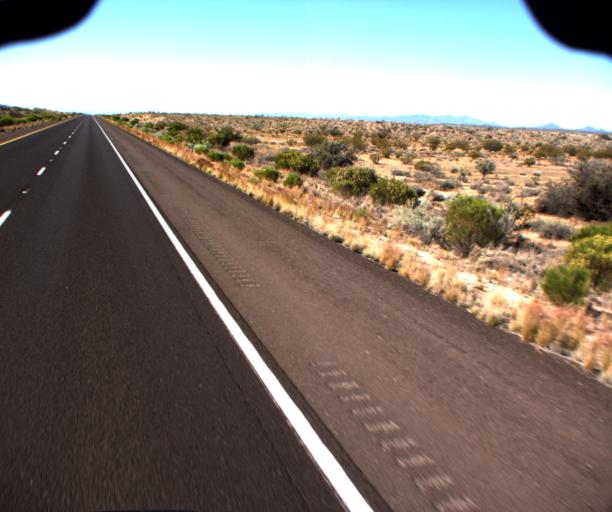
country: US
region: Arizona
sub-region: Mohave County
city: Kingman
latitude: 35.1188
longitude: -113.6669
